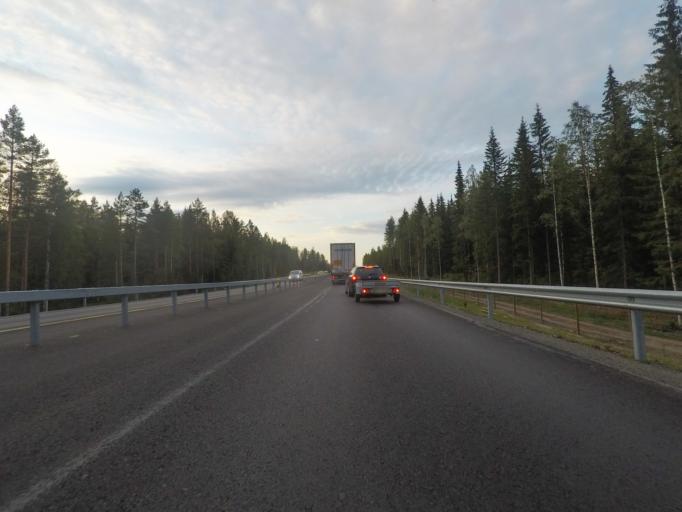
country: FI
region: Central Finland
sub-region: Joutsa
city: Leivonmaeki
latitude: 61.8435
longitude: 26.0987
